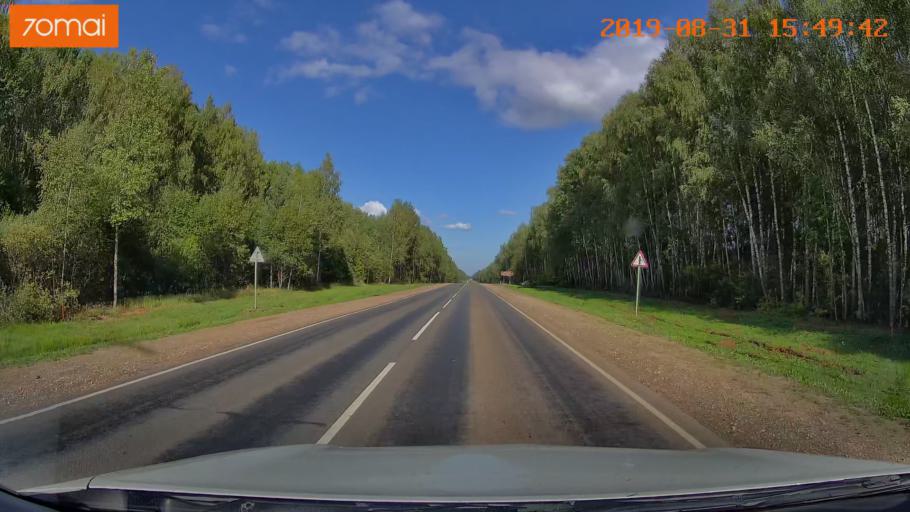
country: RU
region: Kaluga
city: Yukhnov
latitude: 54.6923
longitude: 35.0552
